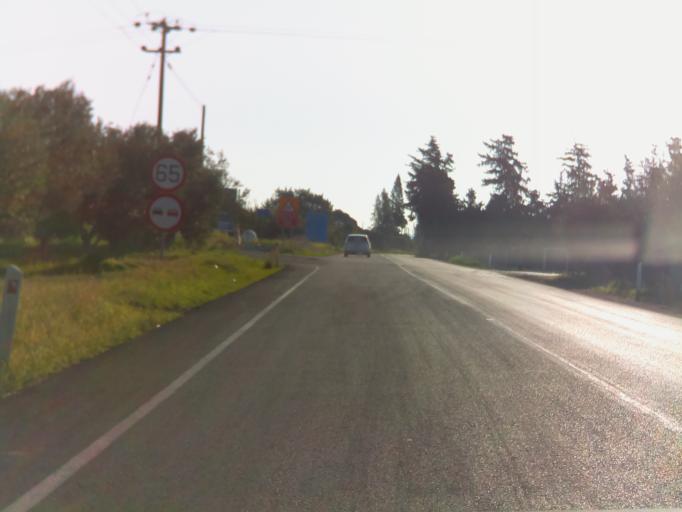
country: CY
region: Pafos
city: Paphos
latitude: 34.7305
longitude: 32.5080
